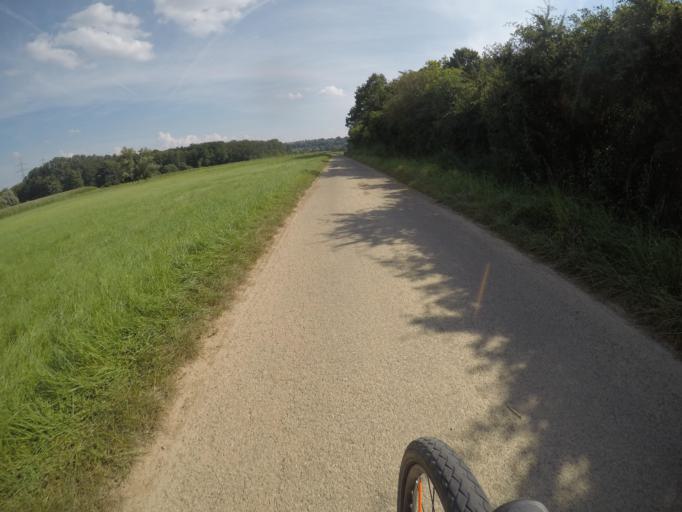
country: DE
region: Baden-Wuerttemberg
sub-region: Karlsruhe Region
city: Olbronn-Durrn
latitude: 48.9703
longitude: 8.7517
